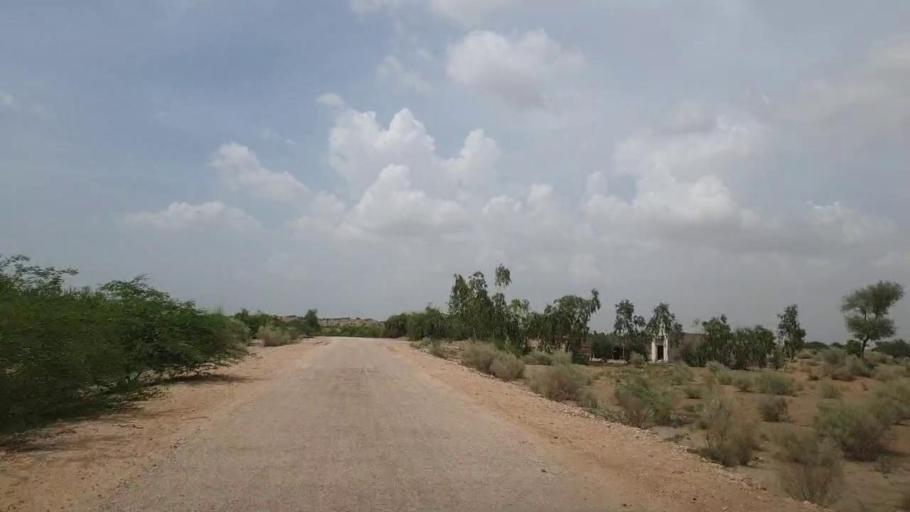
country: PK
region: Sindh
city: Kot Diji
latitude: 27.2451
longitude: 69.0782
